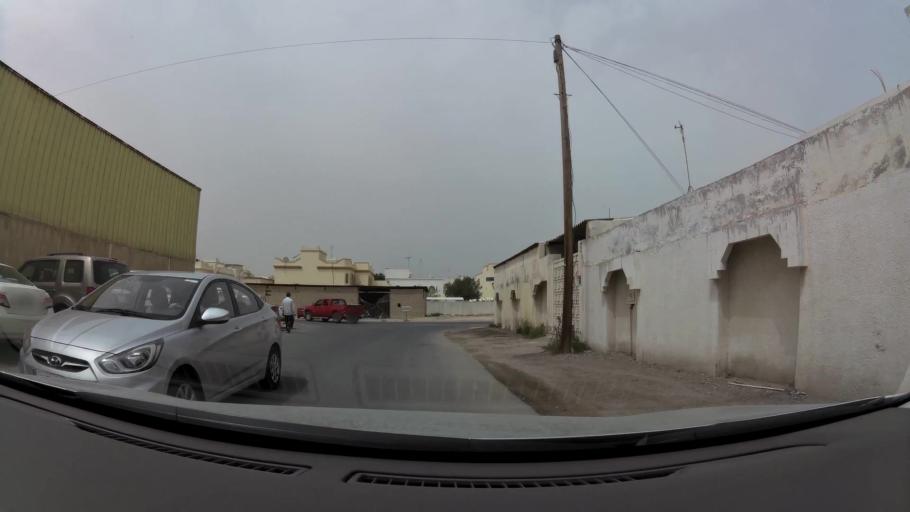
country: QA
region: Baladiyat ad Dawhah
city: Doha
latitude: 25.2476
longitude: 51.5660
